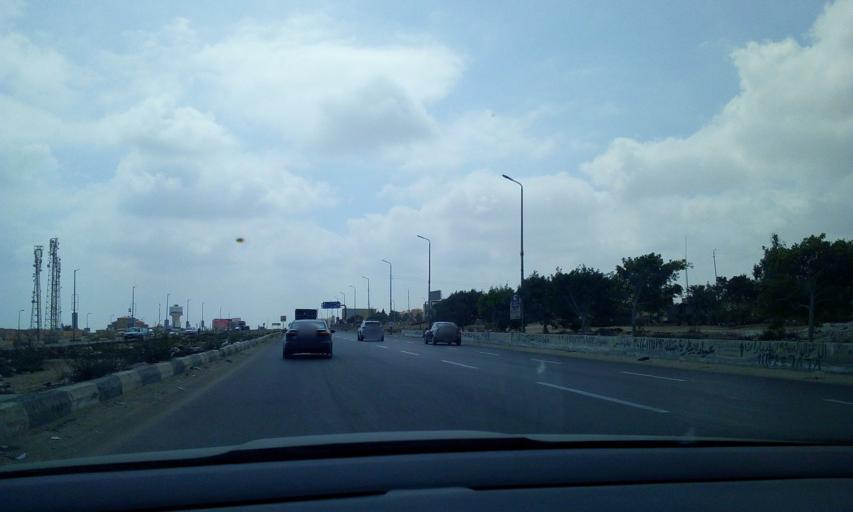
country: EG
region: Muhafazat Matruh
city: Al `Alamayn
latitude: 30.8379
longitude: 28.9551
